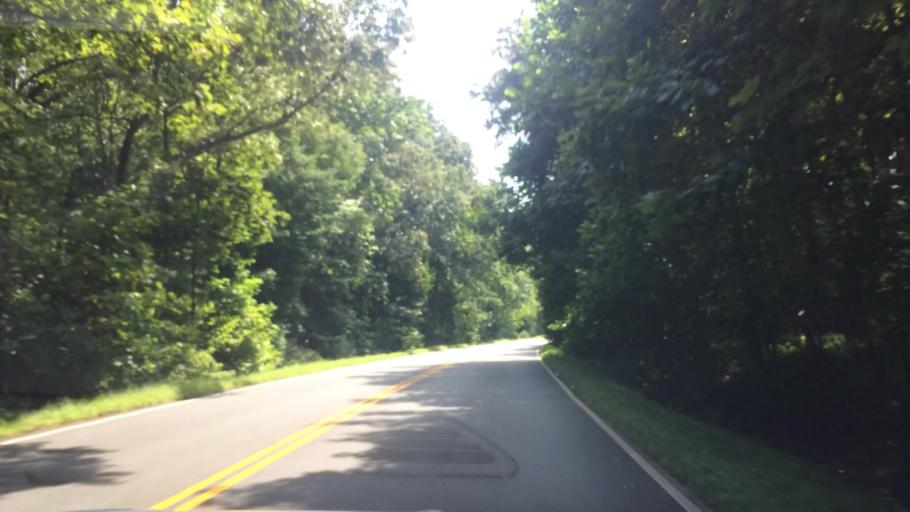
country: US
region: Virginia
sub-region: York County
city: Yorktown
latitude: 37.1694
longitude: -76.4443
